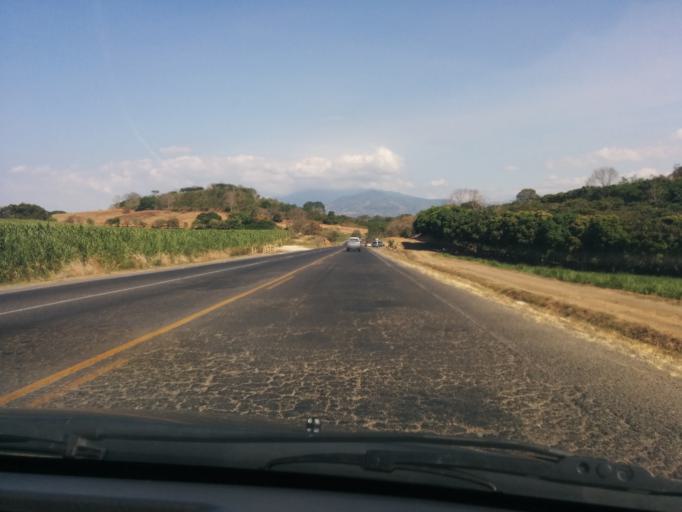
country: CR
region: Alajuela
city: Carrillos
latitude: 10.0076
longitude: -84.3222
